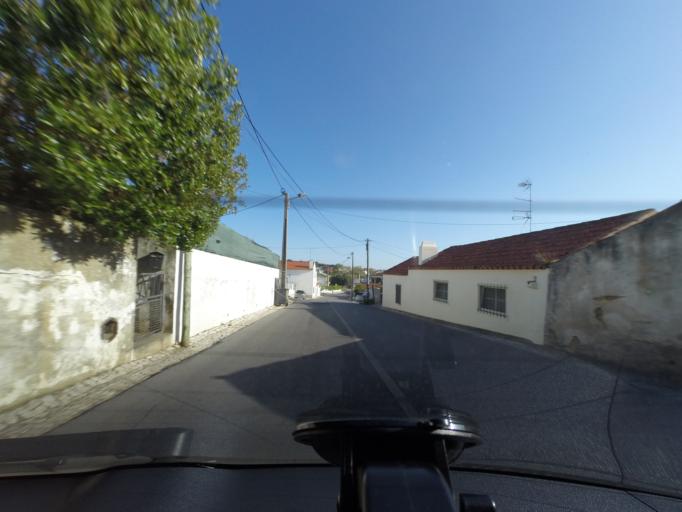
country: PT
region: Lisbon
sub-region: Cascais
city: Alcabideche
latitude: 38.7345
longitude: -9.4395
